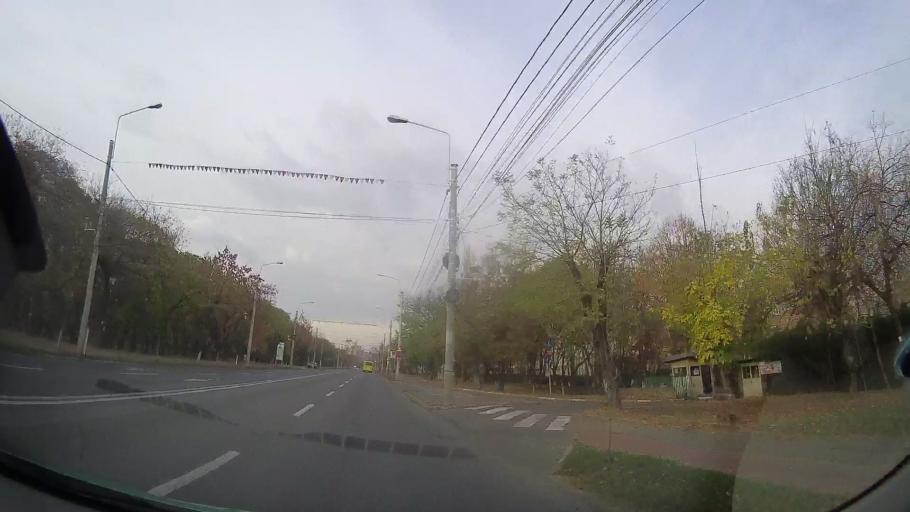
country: RO
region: Prahova
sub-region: Comuna Barcanesti
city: Tatarani
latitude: 44.9127
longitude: 26.0367
